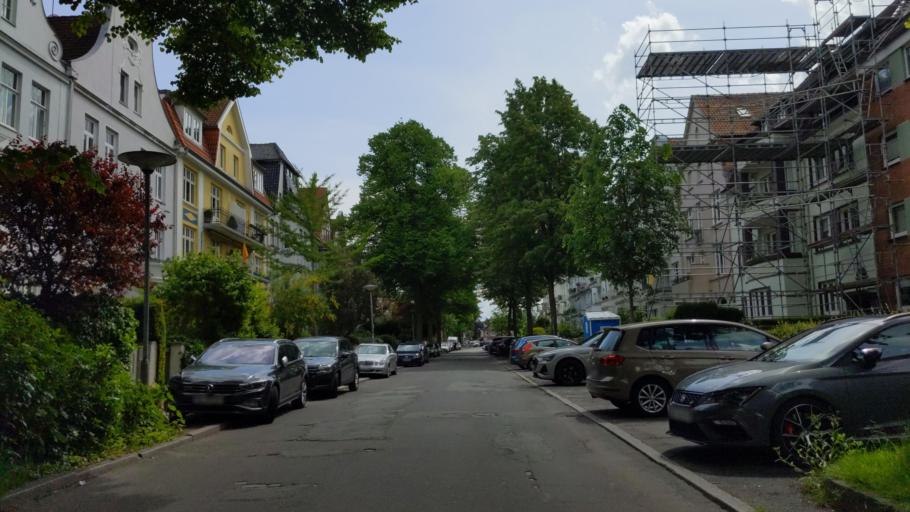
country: DE
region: Schleswig-Holstein
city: Luebeck
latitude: 53.8574
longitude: 10.6979
